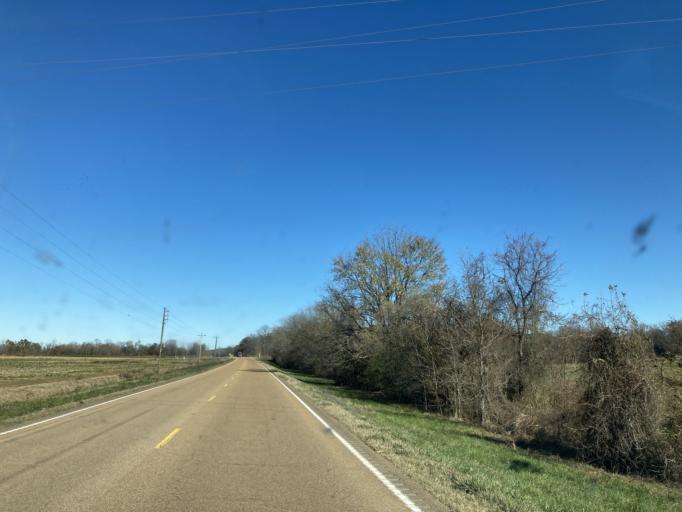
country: US
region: Mississippi
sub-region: Hinds County
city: Lynchburg
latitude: 32.6220
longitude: -90.5747
